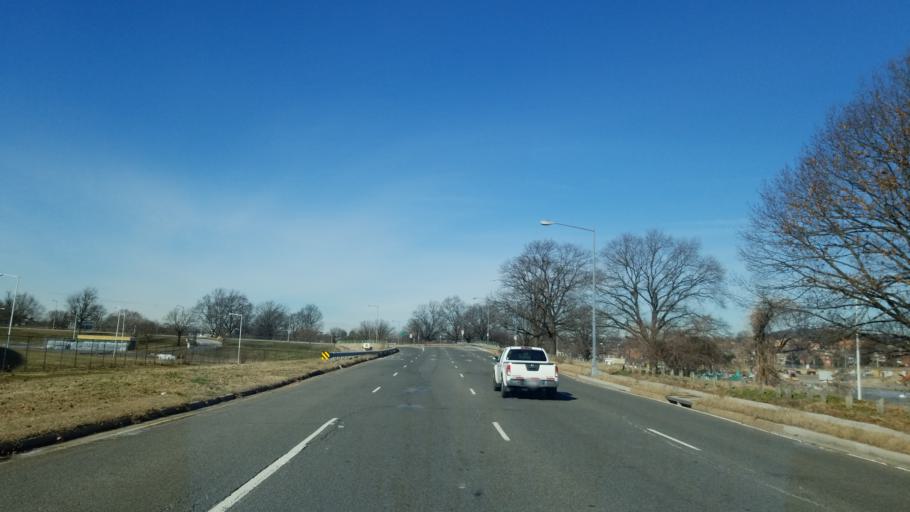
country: US
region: Maryland
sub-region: Prince George's County
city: Colmar Manor
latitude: 38.8908
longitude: -76.9705
